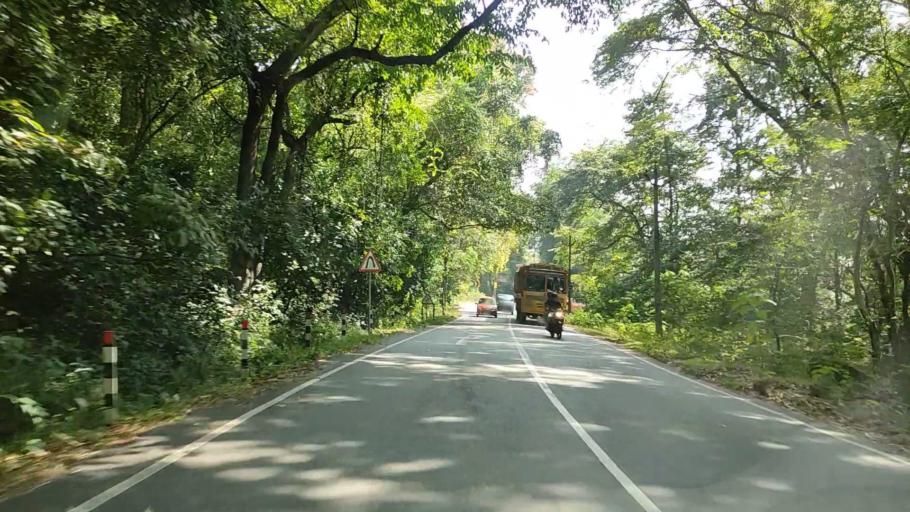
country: IN
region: Kerala
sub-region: Kollam
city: Punalur
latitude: 8.9608
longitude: 77.0681
